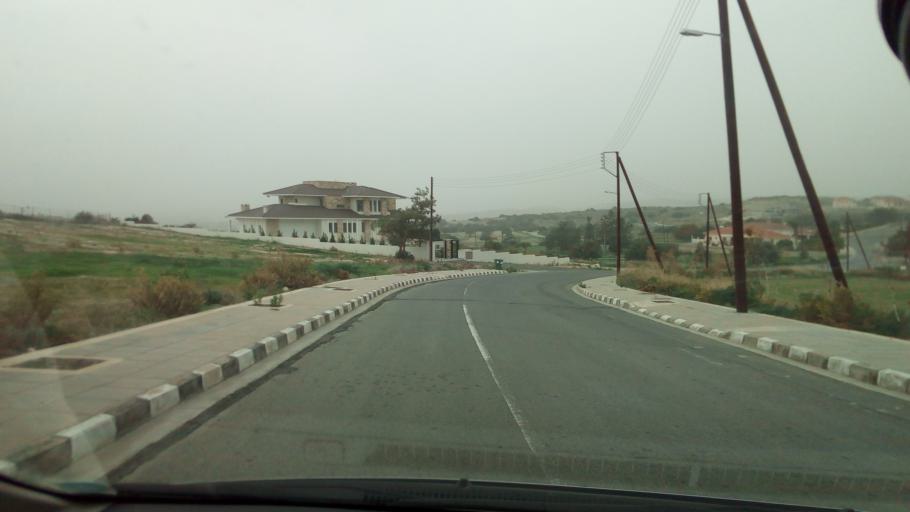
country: CY
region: Larnaka
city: Kofinou
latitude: 34.7640
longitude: 33.3450
